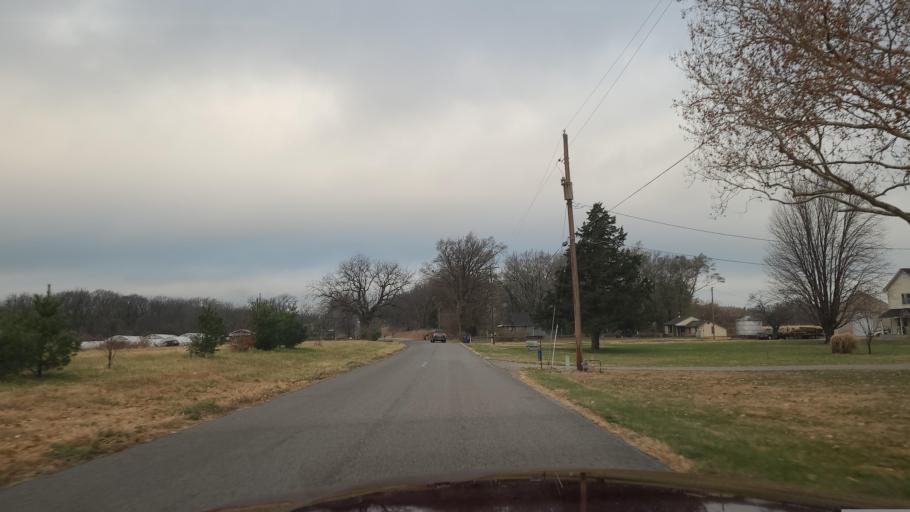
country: US
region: Kansas
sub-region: Douglas County
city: Lawrence
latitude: 38.9641
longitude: -95.2101
